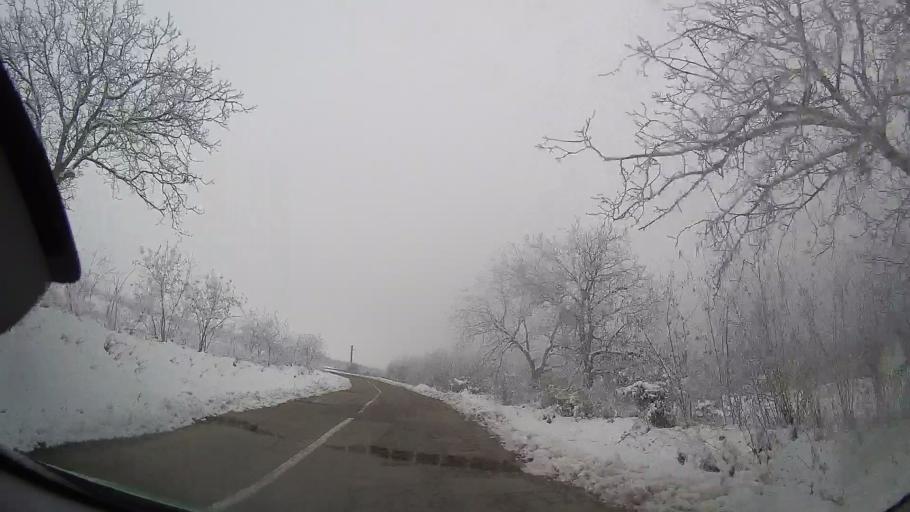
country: RO
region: Neamt
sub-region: Comuna Valea Ursului
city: Valea Ursului
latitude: 46.8048
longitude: 27.0931
